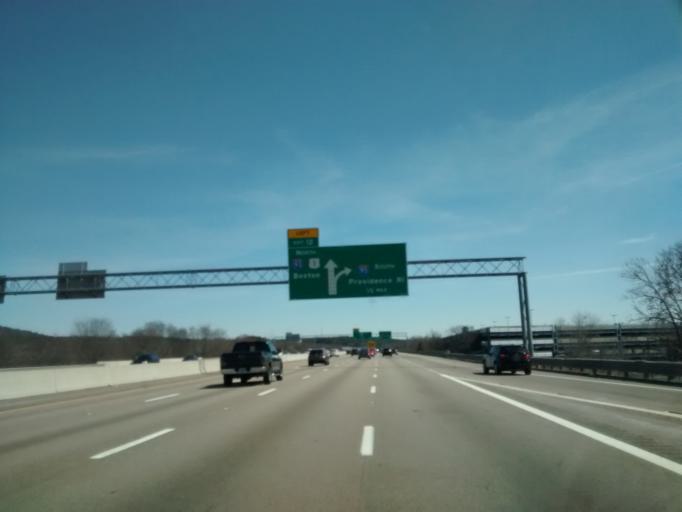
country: US
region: Massachusetts
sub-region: Norfolk County
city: Dedham
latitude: 42.2132
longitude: -71.1504
